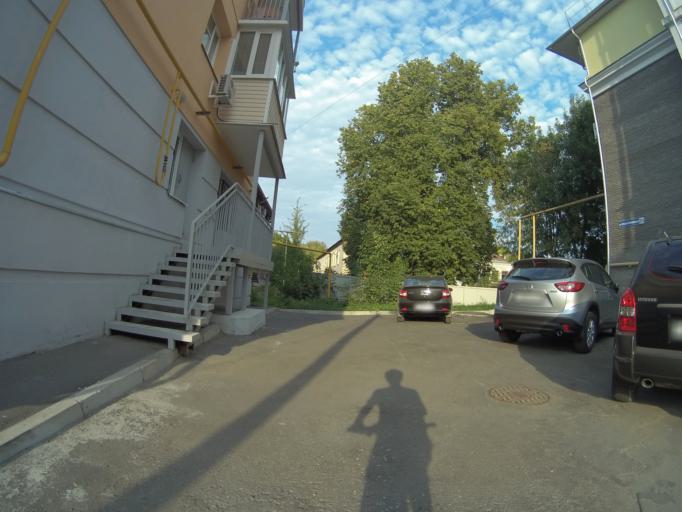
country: RU
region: Vladimir
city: Vladimir
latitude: 56.1365
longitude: 40.4256
